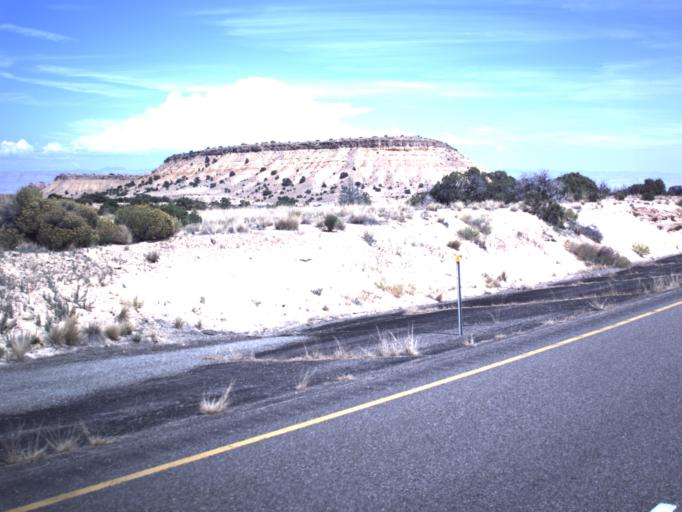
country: US
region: Utah
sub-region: Emery County
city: Castle Dale
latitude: 38.9131
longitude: -110.5086
